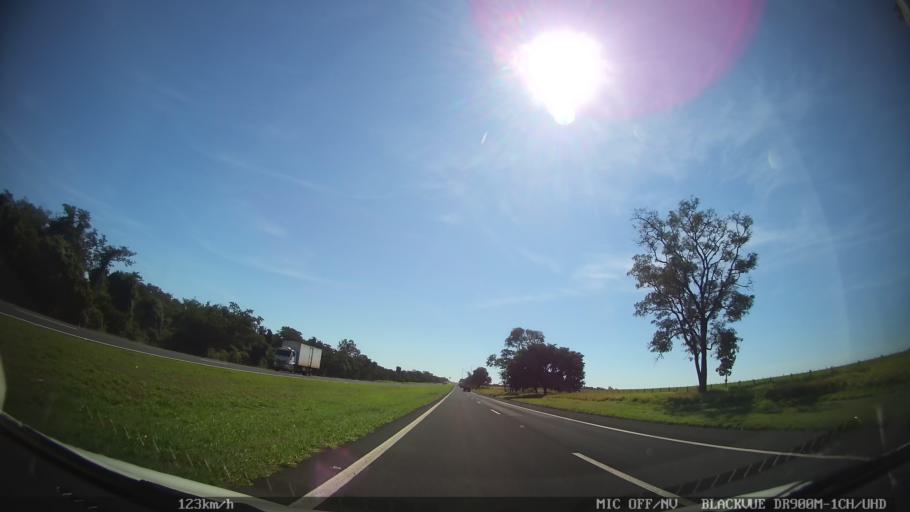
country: BR
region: Sao Paulo
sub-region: Santa Rita Do Passa Quatro
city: Santa Rita do Passa Quatro
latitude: -21.6360
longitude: -47.6126
